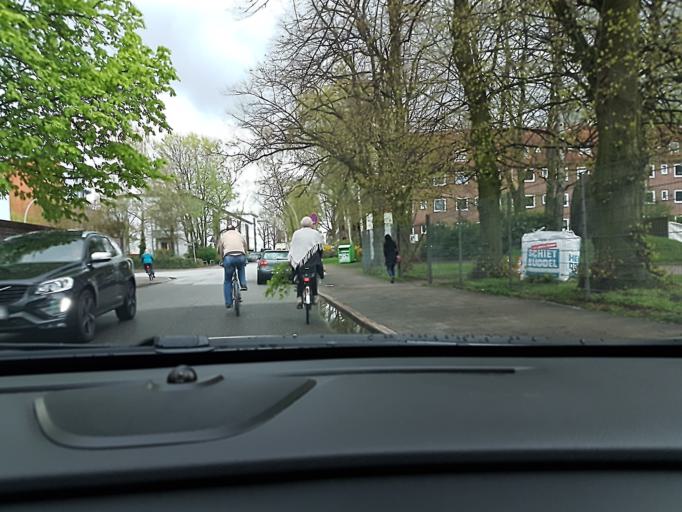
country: DE
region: Hamburg
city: Altona
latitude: 53.5561
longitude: 9.9105
